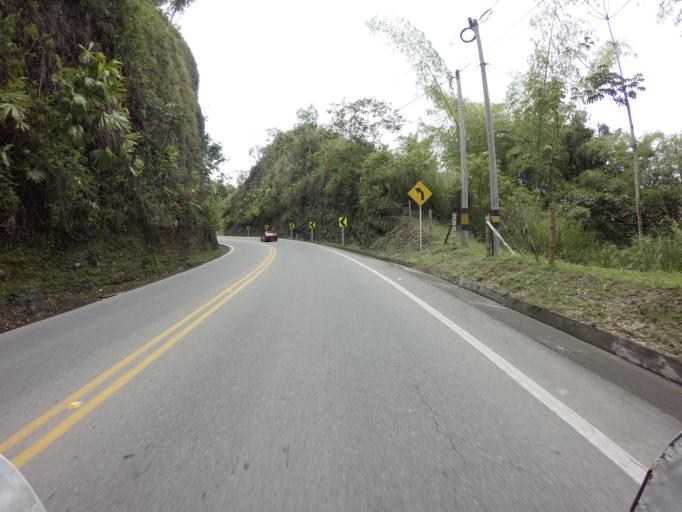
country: CO
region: Quindio
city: Quimbaya
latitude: 4.6108
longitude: -75.7758
